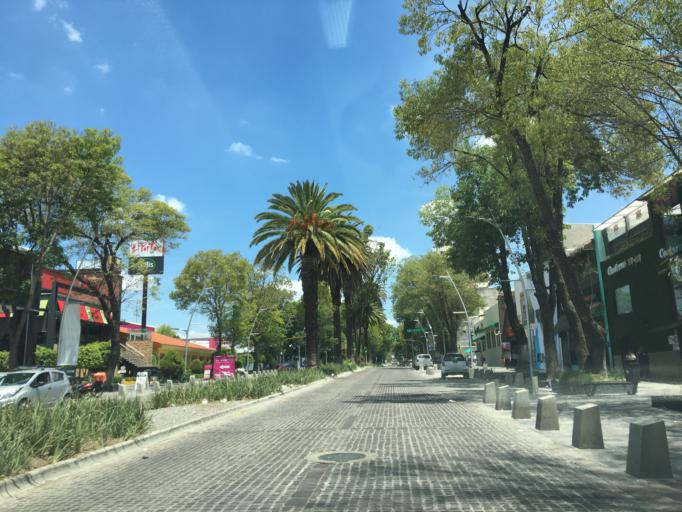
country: MX
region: Puebla
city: Puebla
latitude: 19.0494
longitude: -98.2139
